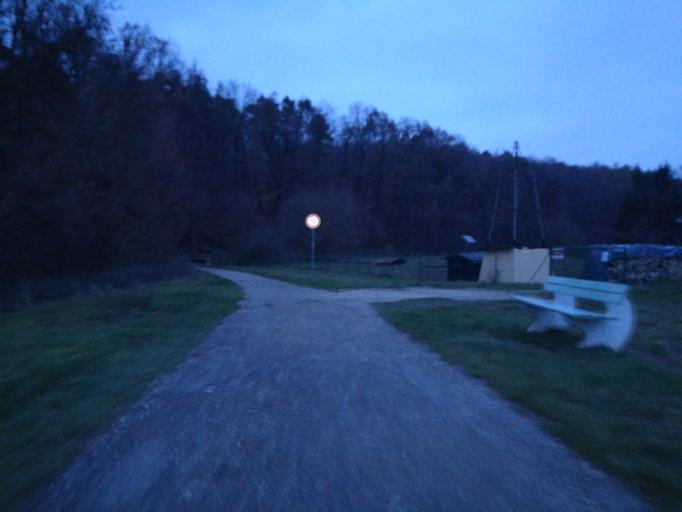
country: DE
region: Bavaria
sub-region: Regierungsbezirk Mittelfranken
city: Seukendorf
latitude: 49.4847
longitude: 10.9007
